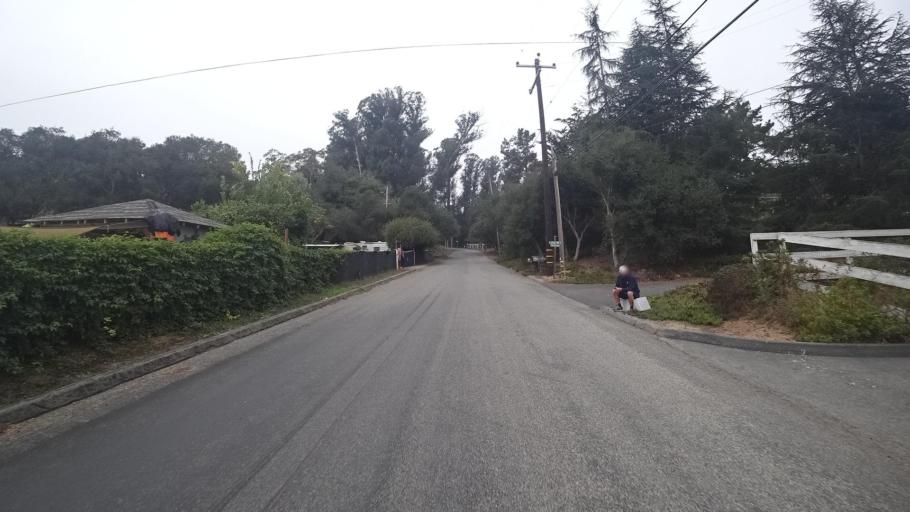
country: US
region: California
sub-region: San Benito County
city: Aromas
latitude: 36.8784
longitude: -121.6424
